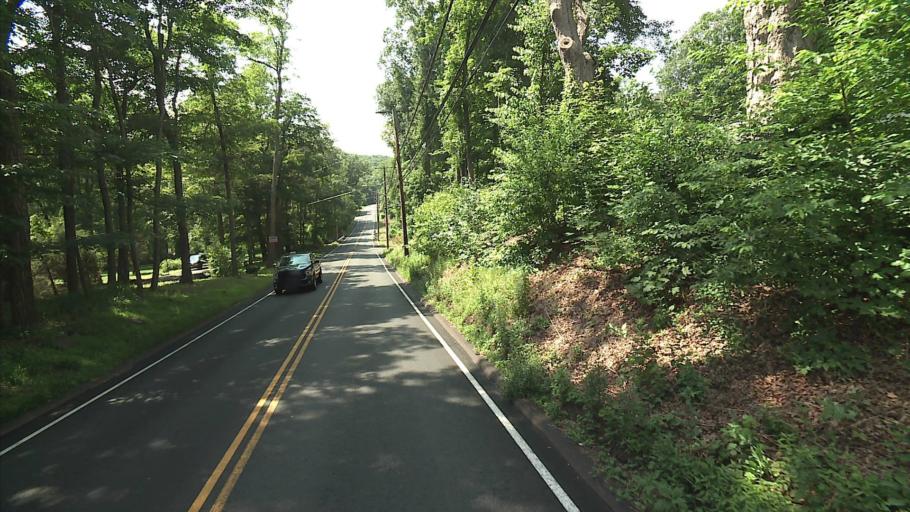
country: US
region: Connecticut
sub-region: New Haven County
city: Branford
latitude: 41.3252
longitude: -72.8139
